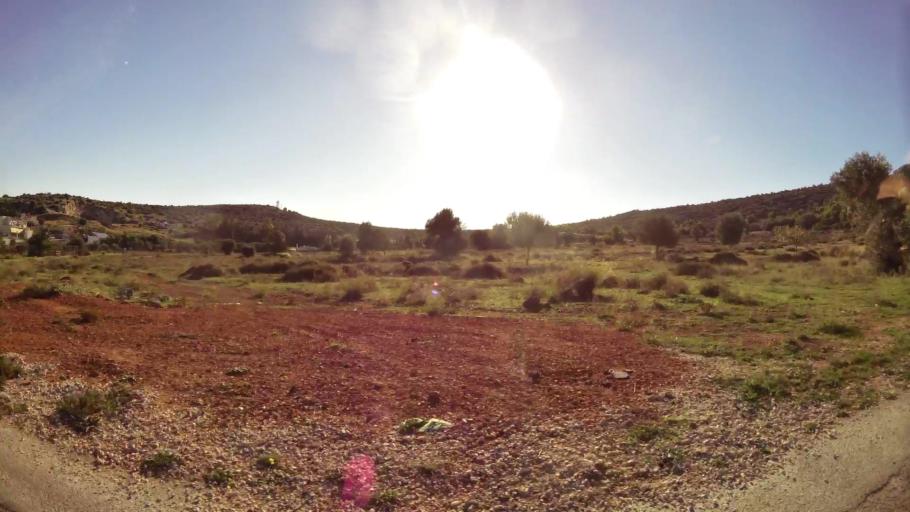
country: GR
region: Attica
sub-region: Nomarchia Anatolikis Attikis
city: Koropi
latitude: 37.8932
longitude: 23.8639
